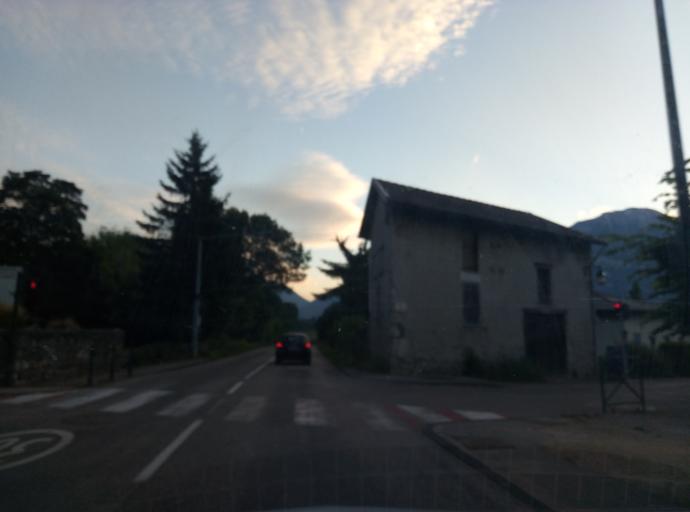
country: FR
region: Rhone-Alpes
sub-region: Departement de l'Isere
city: Noyarey
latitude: 45.2437
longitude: 5.6323
